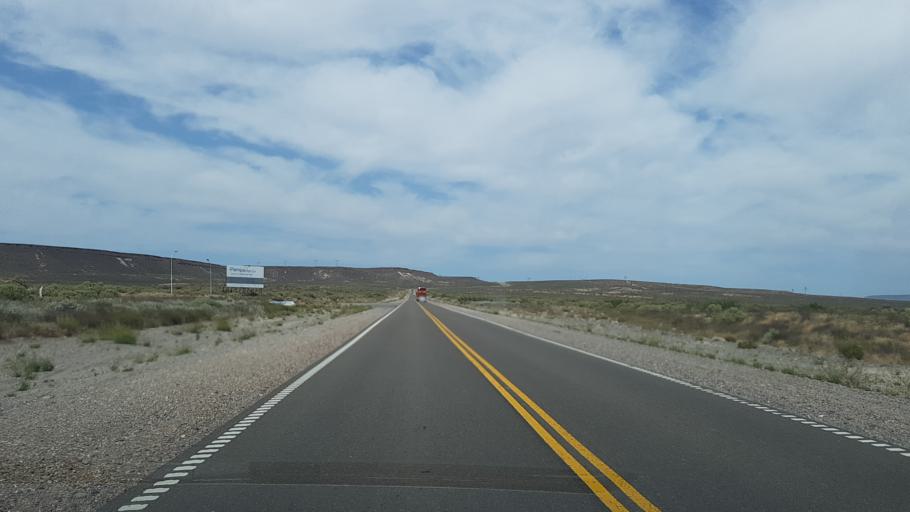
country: AR
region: Neuquen
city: Piedra del Aguila
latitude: -39.9619
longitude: -70.0047
